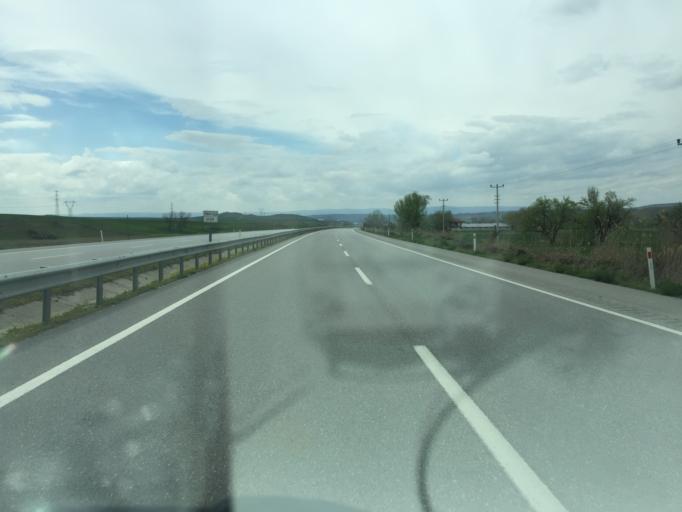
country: TR
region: Corum
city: Sungurlu
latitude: 40.1428
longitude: 34.2776
